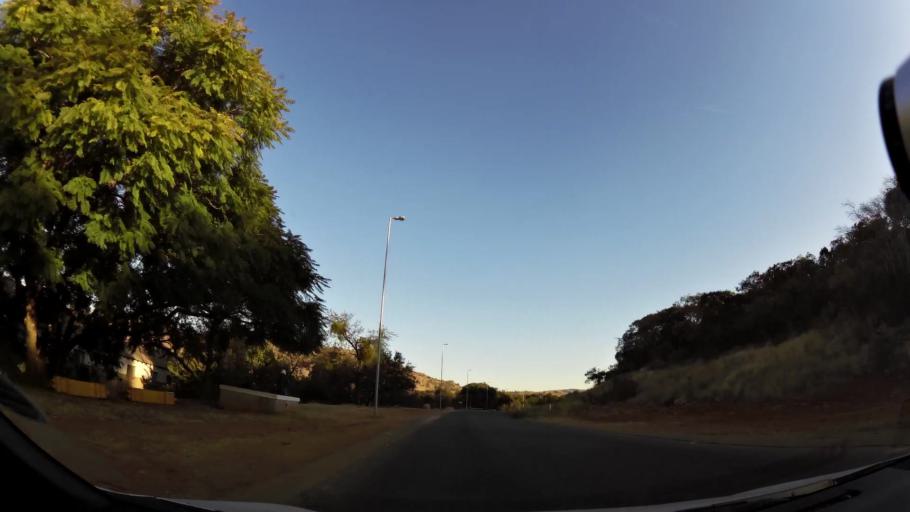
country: ZA
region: North-West
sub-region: Bojanala Platinum District Municipality
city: Rustenburg
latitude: -25.7127
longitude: 27.2401
